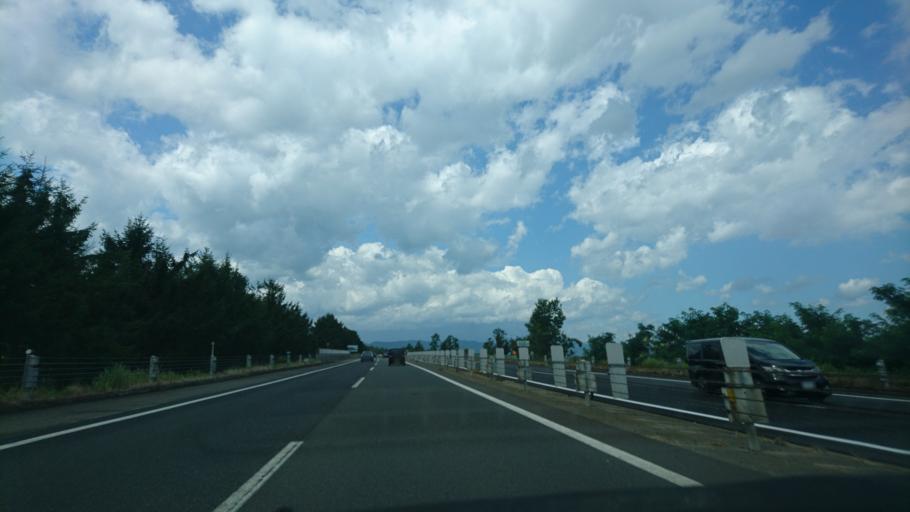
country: JP
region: Iwate
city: Morioka-shi
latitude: 39.6630
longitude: 141.1151
